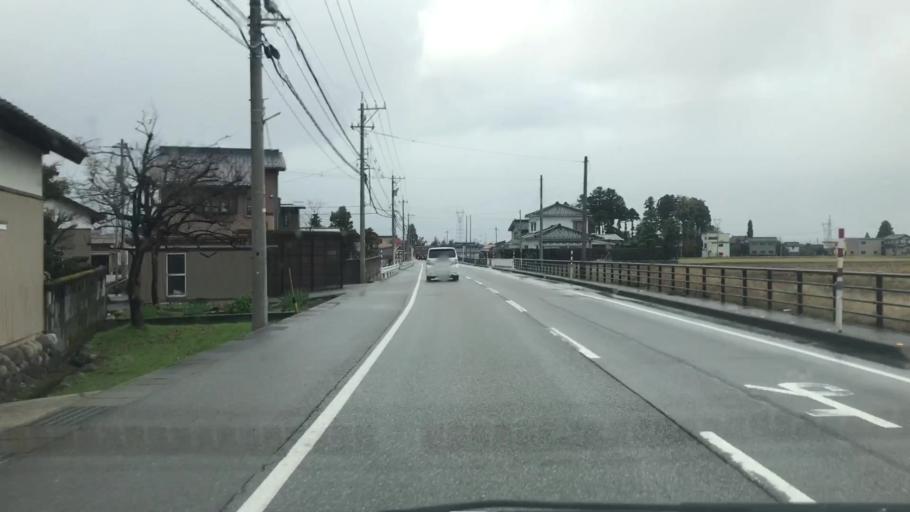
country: JP
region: Toyama
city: Kamiichi
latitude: 36.6760
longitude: 137.2903
